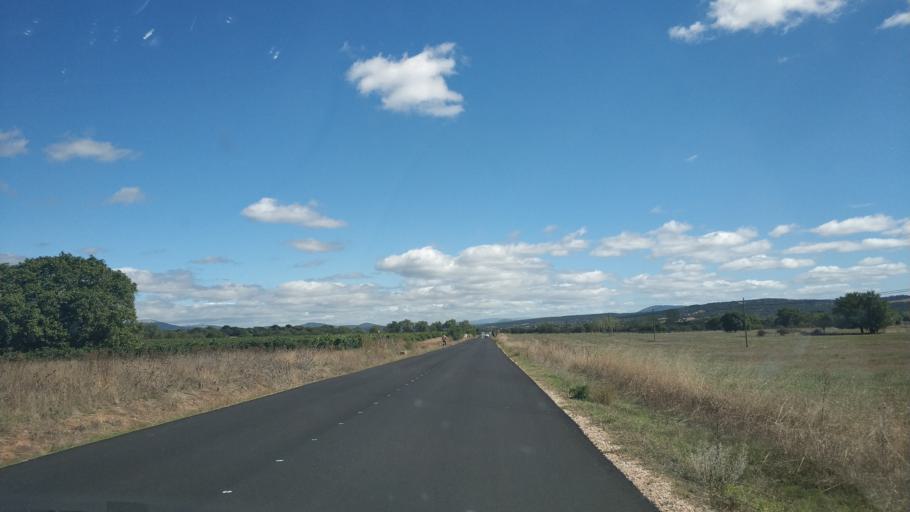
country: ES
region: Castille and Leon
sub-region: Provincia de Burgos
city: Puentedura
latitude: 42.0329
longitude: -3.6404
